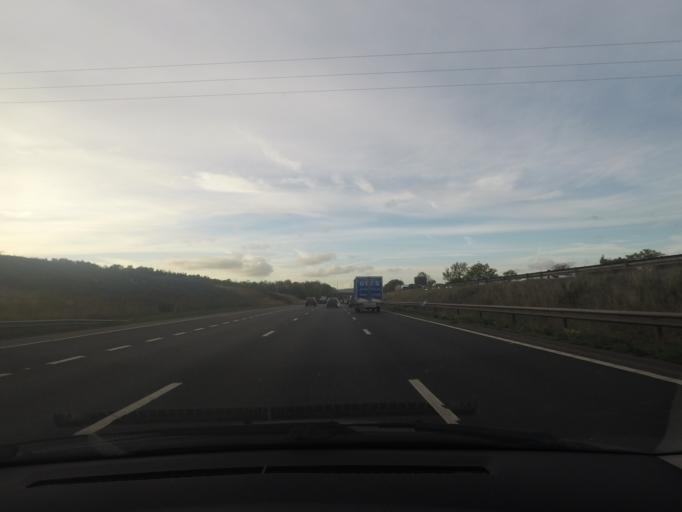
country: GB
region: England
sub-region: Barnsley
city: Dodworth
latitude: 53.5535
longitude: -1.5237
